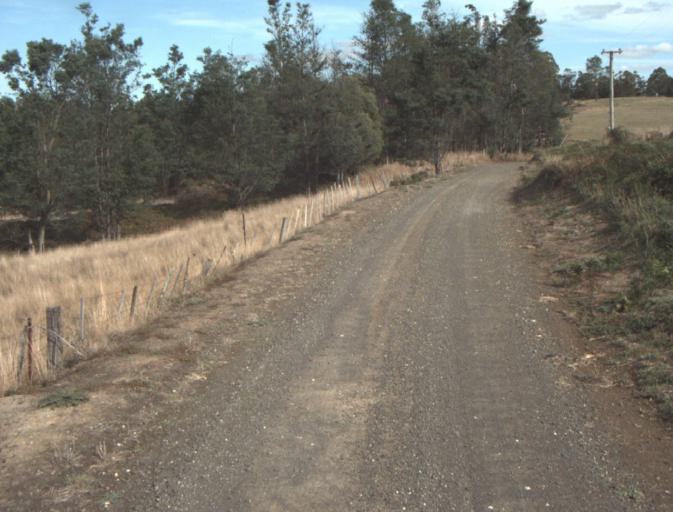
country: AU
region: Tasmania
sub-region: Launceston
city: Mayfield
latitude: -41.1954
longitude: 147.1952
